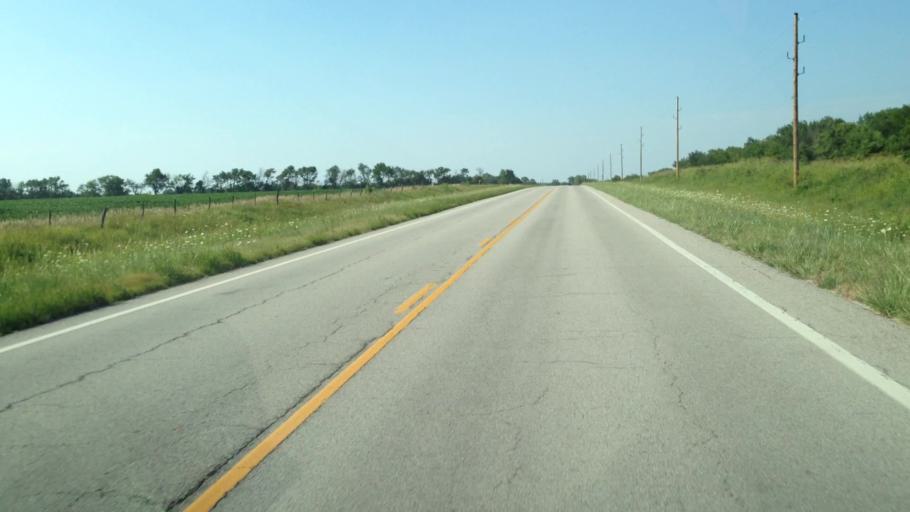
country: US
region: Kansas
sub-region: Allen County
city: Iola
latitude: 38.0118
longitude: -95.1709
